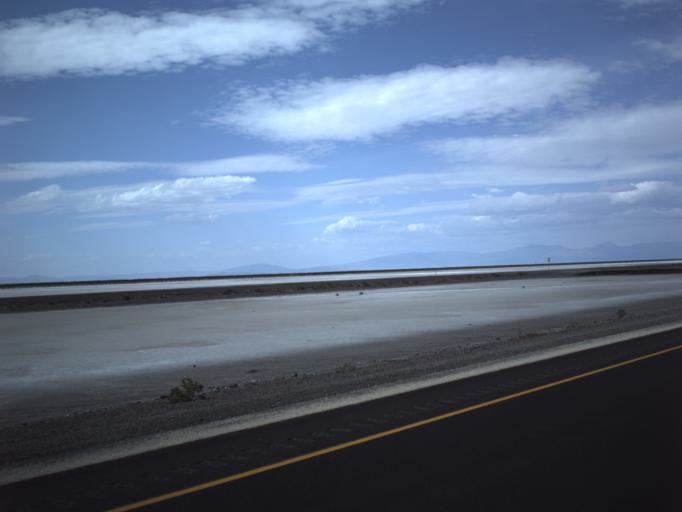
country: US
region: Utah
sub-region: Tooele County
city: Wendover
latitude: 40.7339
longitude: -113.5918
